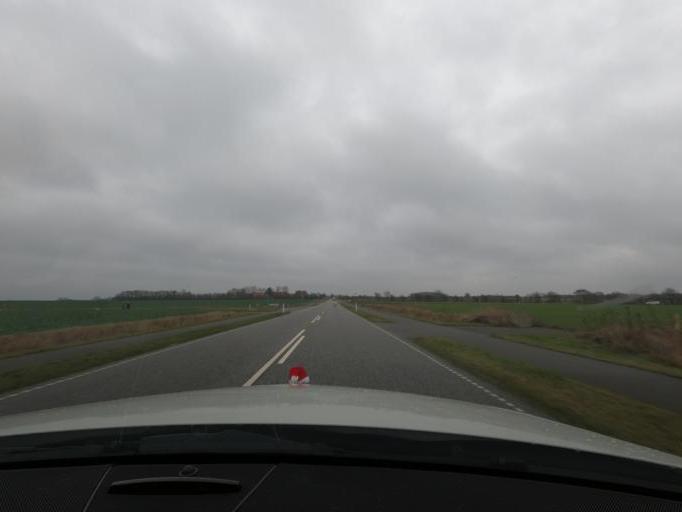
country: DK
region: South Denmark
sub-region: Haderslev Kommune
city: Starup
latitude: 55.2545
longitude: 9.6837
